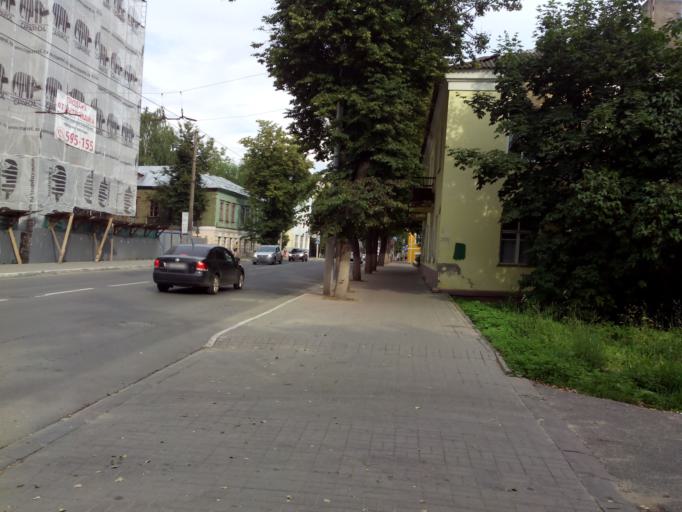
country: RU
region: Kaluga
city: Kaluga
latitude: 54.5148
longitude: 36.2356
